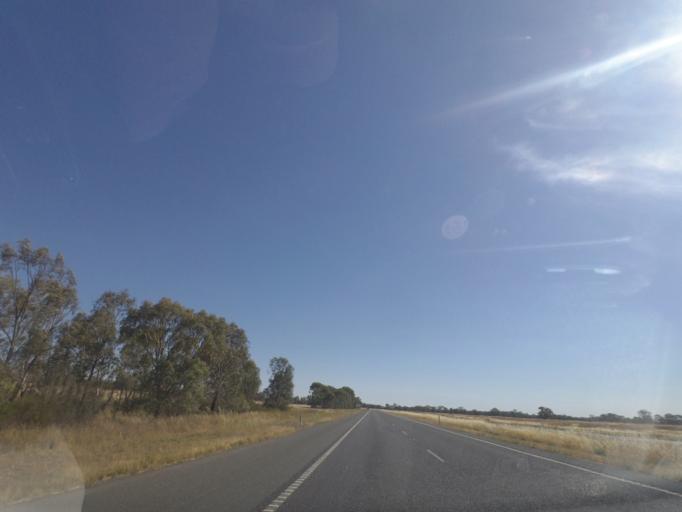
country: AU
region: Victoria
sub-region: Greater Shepparton
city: Shepparton
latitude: -36.6321
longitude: 145.2945
